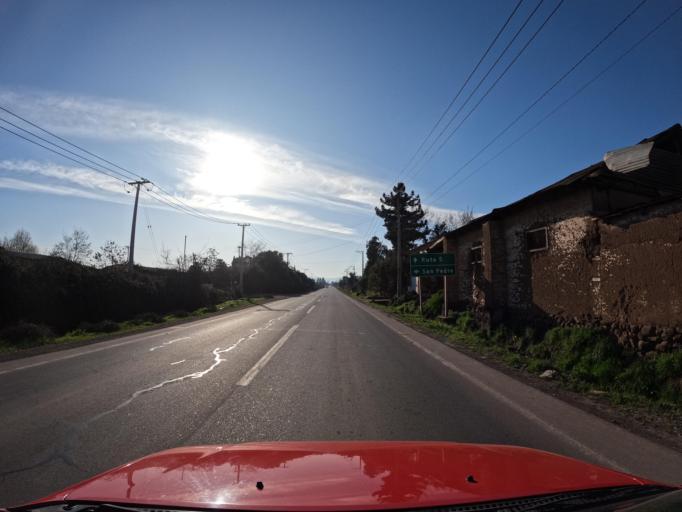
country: CL
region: Maule
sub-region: Provincia de Curico
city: Teno
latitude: -34.8917
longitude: -71.0670
